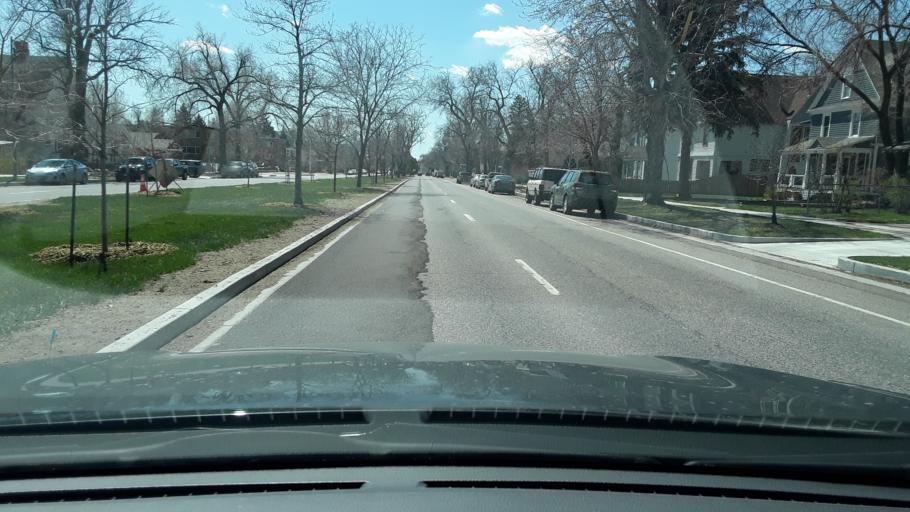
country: US
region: Colorado
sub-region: El Paso County
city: Colorado Springs
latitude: 38.8535
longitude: -104.8207
